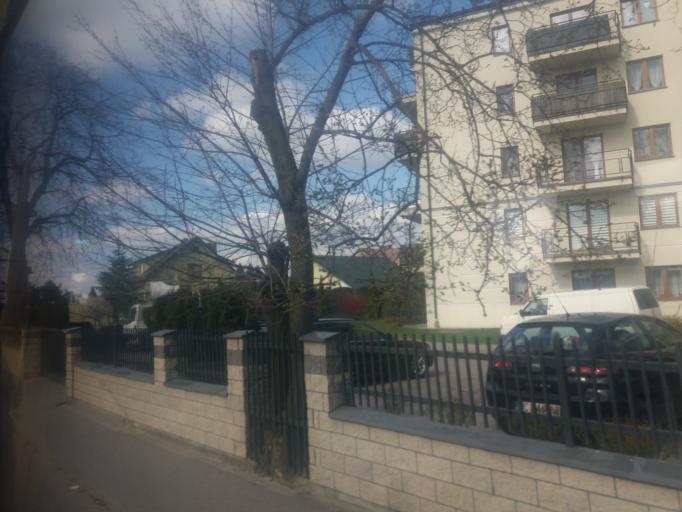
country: PL
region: Masovian Voivodeship
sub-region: Powiat mlawski
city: Mlawa
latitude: 53.1247
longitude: 20.3599
